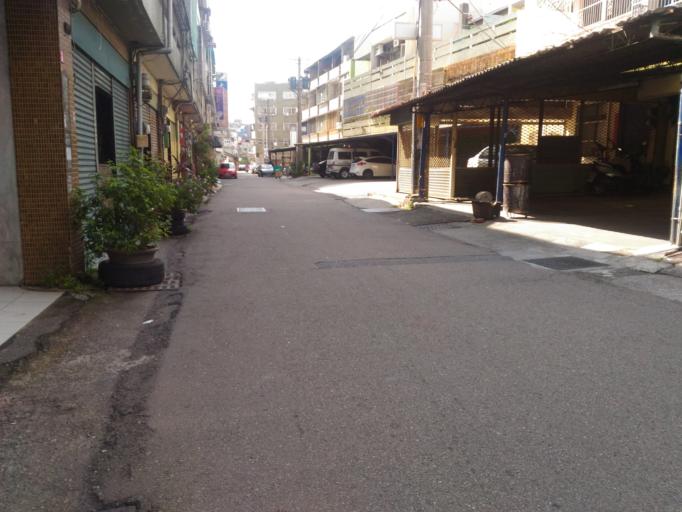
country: TW
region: Taiwan
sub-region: Changhua
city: Chang-hua
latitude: 24.0847
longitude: 120.5597
